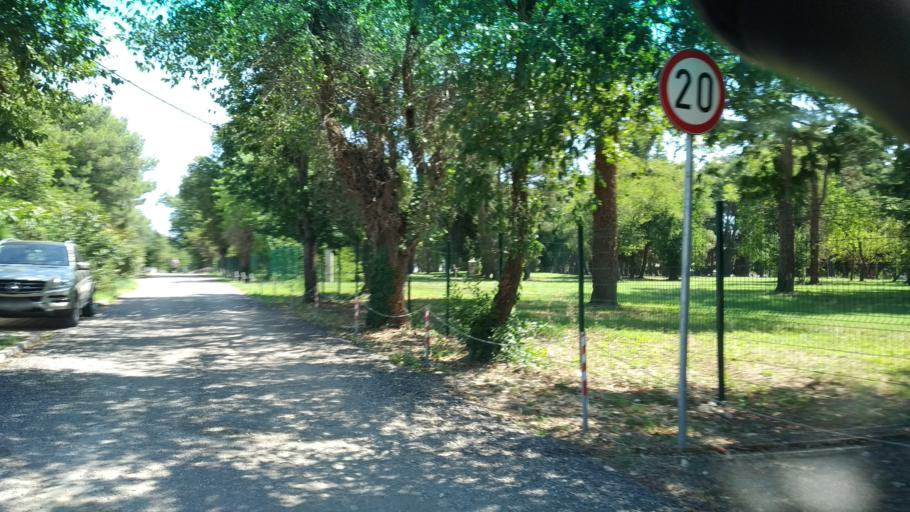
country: HR
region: Istarska
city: Fazana
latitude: 44.9212
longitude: 13.8029
